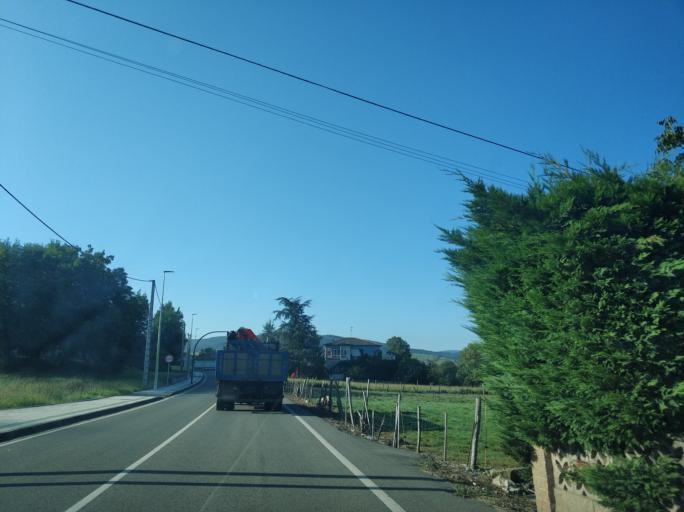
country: ES
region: Cantabria
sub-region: Provincia de Cantabria
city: Polanco
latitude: 43.3654
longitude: -3.9579
